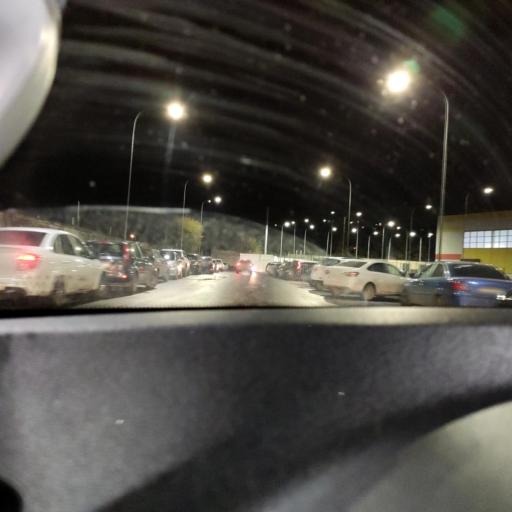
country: RU
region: Samara
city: Smyshlyayevka
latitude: 53.2143
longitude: 50.2843
